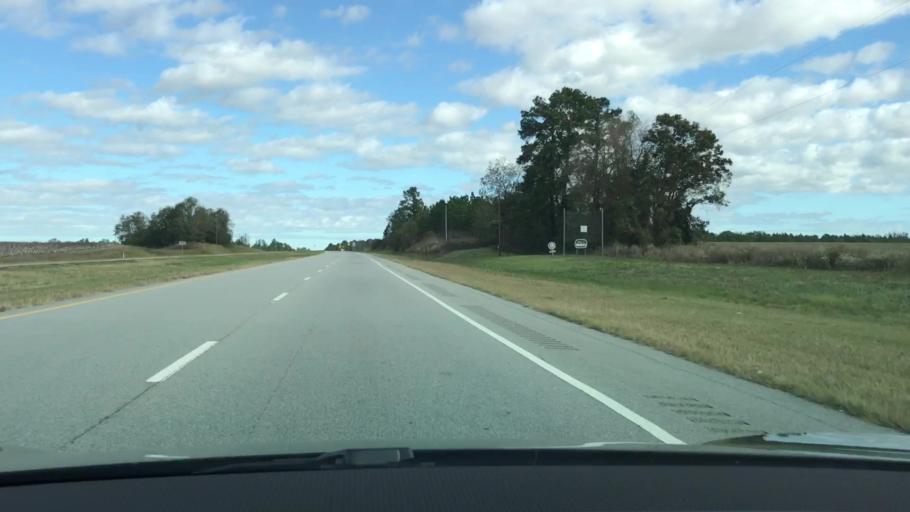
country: US
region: Georgia
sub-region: Jefferson County
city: Wadley
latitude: 32.8383
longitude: -82.3996
